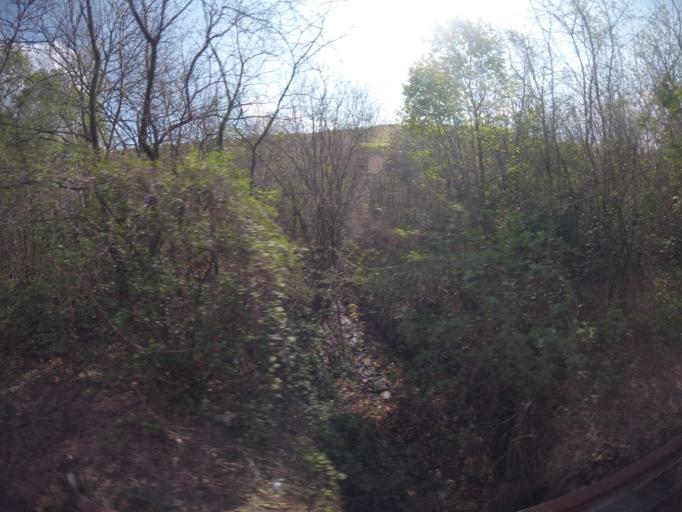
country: IT
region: Piedmont
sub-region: Provincia di Novara
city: Pettenasco
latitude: 45.8398
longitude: 8.4021
